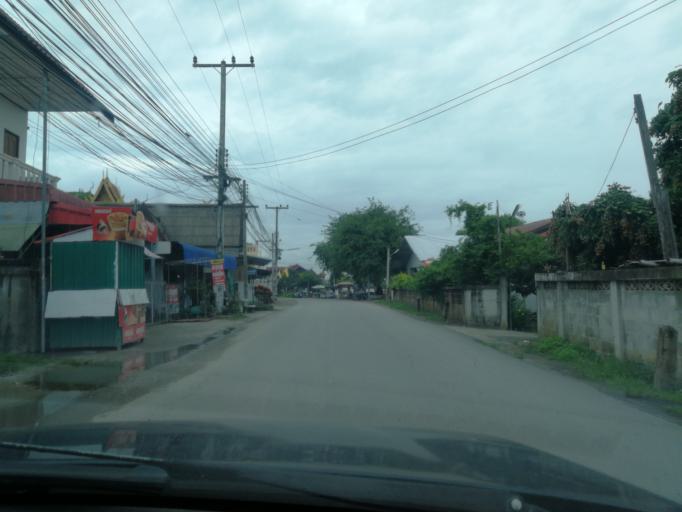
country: TH
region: Chiang Mai
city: San Pa Tong
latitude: 18.5917
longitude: 98.9117
